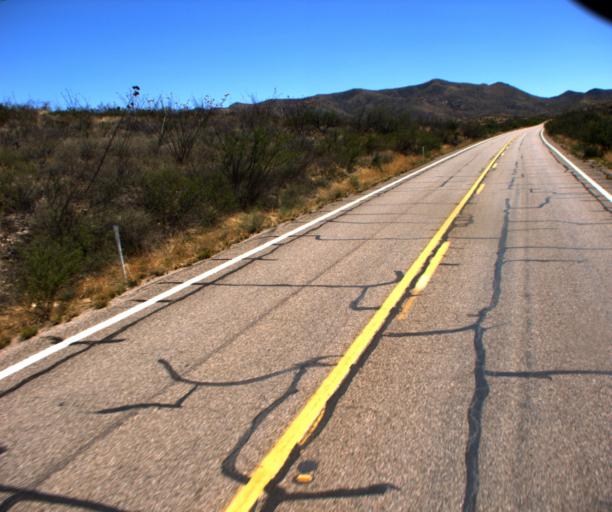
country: US
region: Arizona
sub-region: Pima County
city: Corona de Tucson
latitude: 31.9294
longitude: -110.6584
